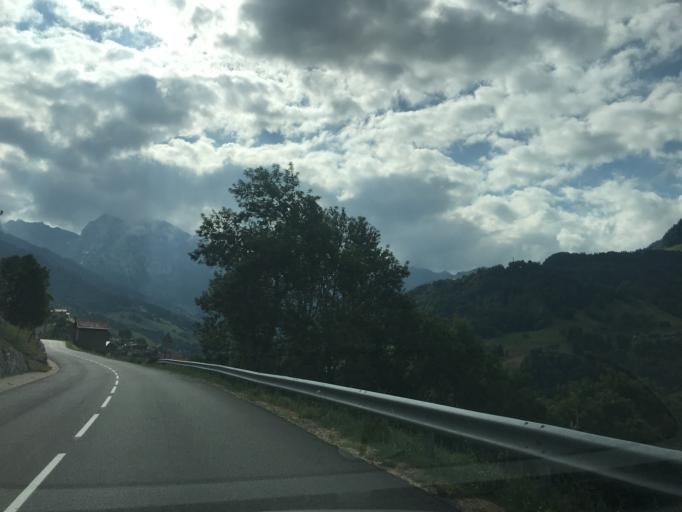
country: FR
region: Rhone-Alpes
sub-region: Departement de la Haute-Savoie
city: Thones
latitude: 45.8608
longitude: 6.3622
